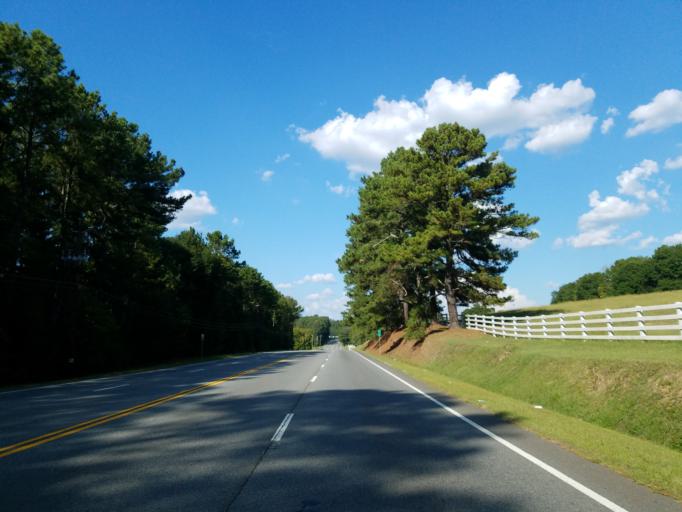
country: US
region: Georgia
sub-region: Bartow County
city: Cartersville
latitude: 34.2255
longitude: -84.7872
